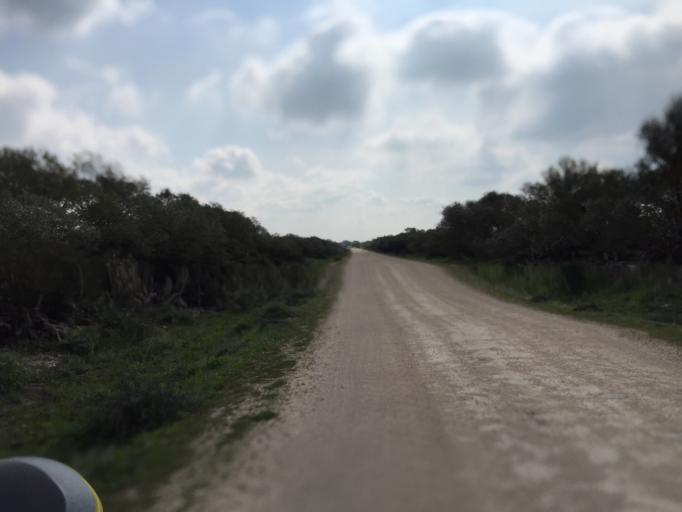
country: ES
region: Andalusia
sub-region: Provincia de Cadiz
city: Benalup-Casas Viejas
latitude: 36.3285
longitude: -5.8901
